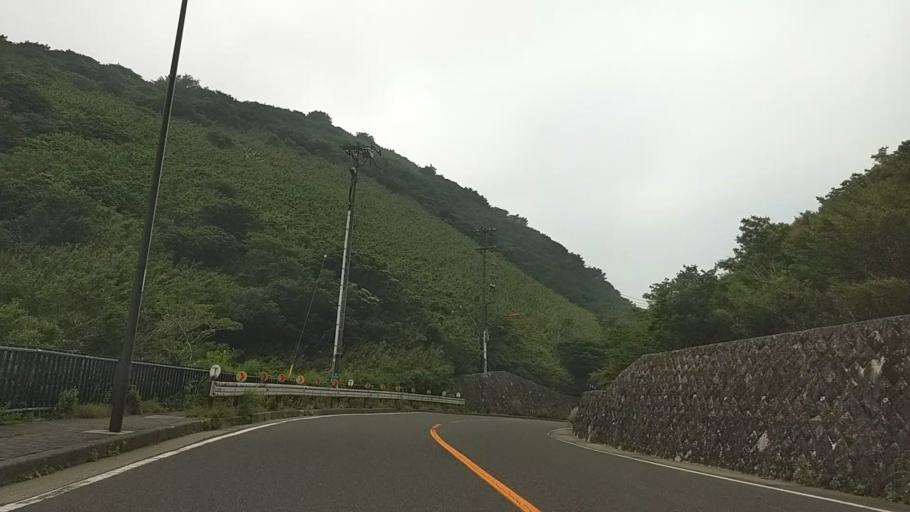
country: JP
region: Kanagawa
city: Hakone
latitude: 35.2152
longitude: 139.0368
